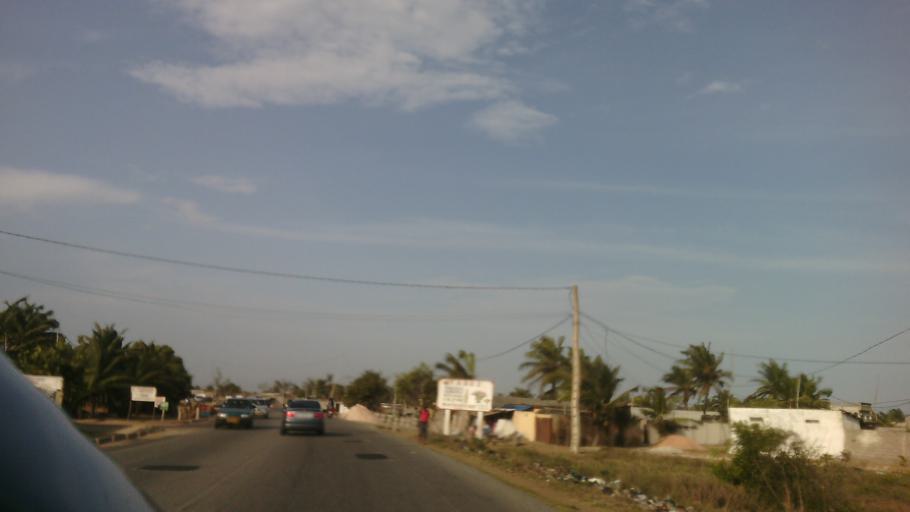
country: TG
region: Maritime
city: Lome
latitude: 6.1814
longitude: 1.3908
